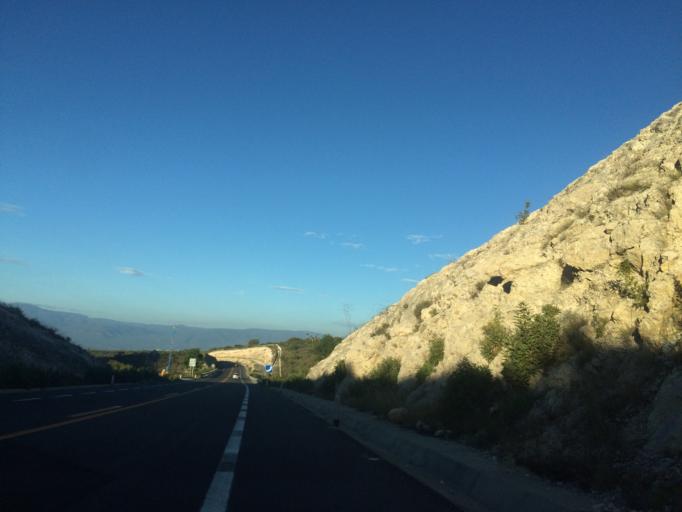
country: MX
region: Puebla
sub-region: Tehuacan
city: Magdalena Cuayucatepec
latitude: 18.6193
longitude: -97.4714
